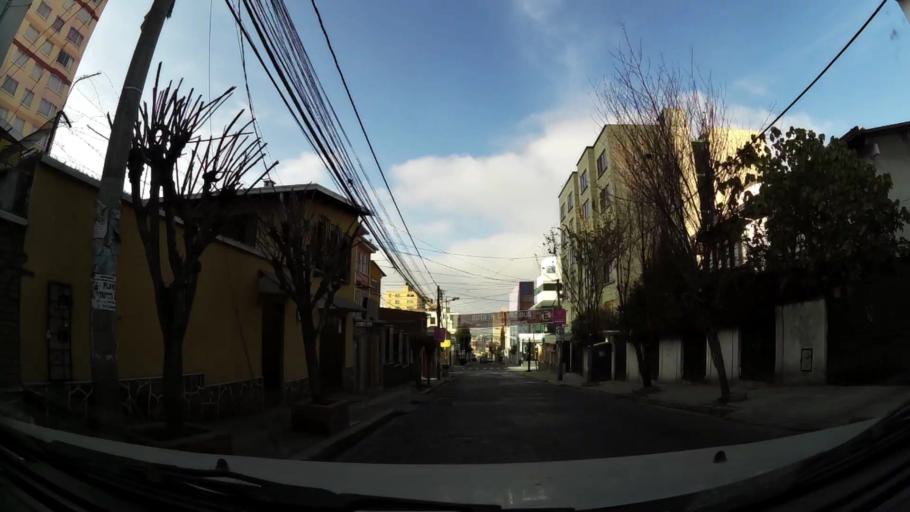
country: BO
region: La Paz
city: La Paz
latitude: -16.4927
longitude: -68.1222
